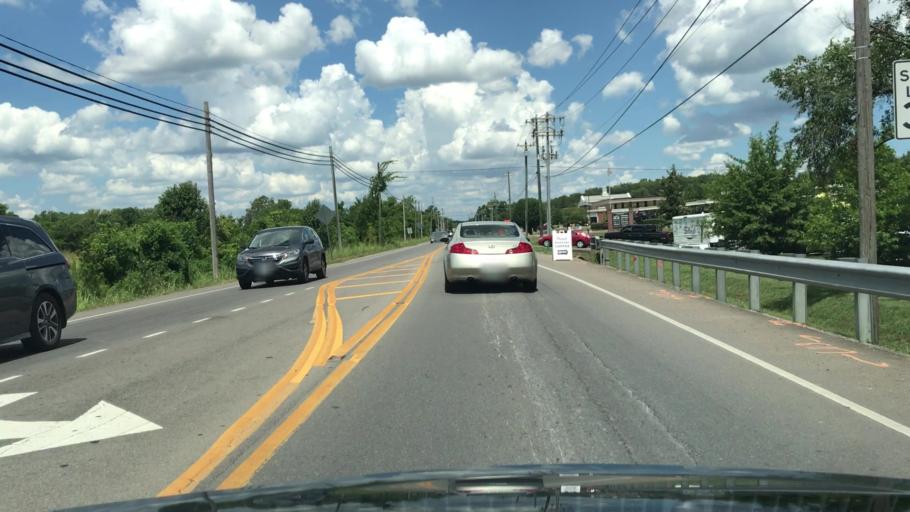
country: US
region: Tennessee
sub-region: Williamson County
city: Nolensville
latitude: 35.9593
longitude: -86.6728
